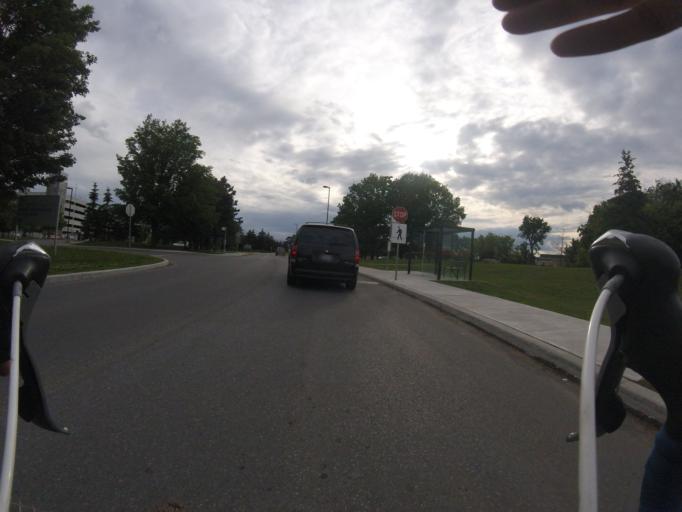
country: CA
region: Ontario
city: Bells Corners
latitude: 45.3371
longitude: -75.8077
